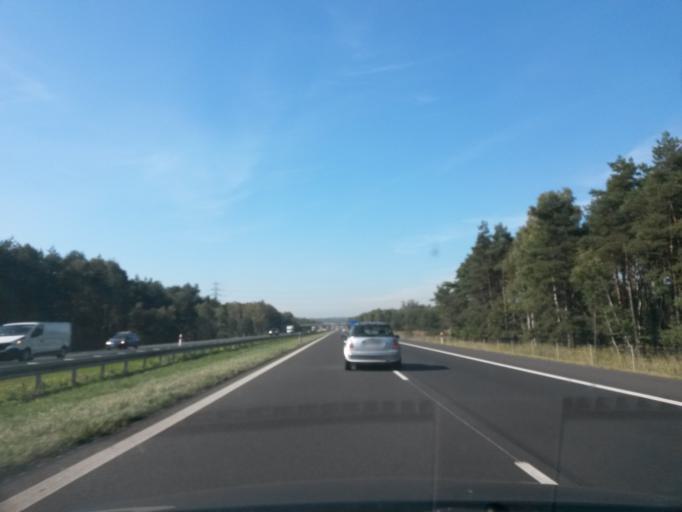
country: PL
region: Lesser Poland Voivodeship
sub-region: Powiat chrzanowski
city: Trzebinia
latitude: 50.1417
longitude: 19.4521
